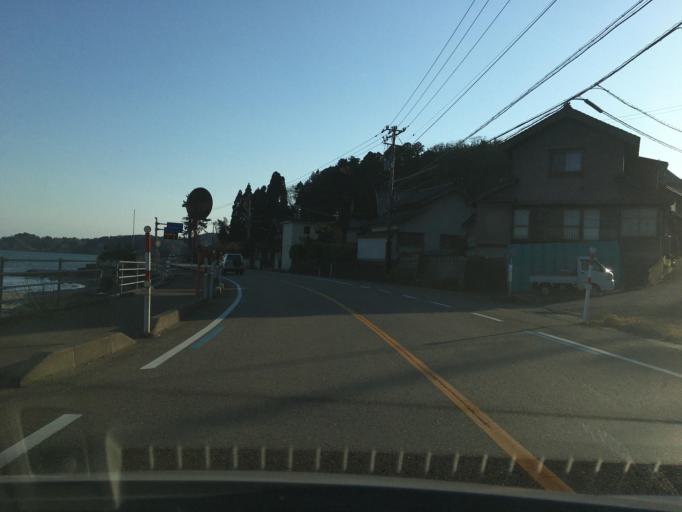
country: JP
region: Toyama
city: Himi
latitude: 36.9492
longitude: 137.0375
